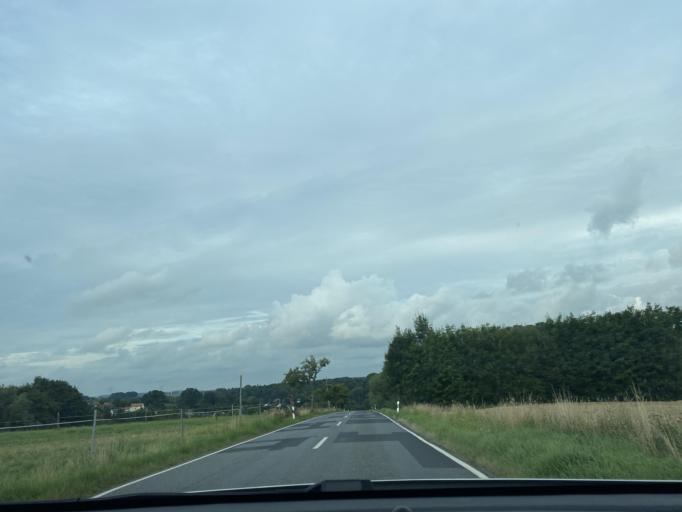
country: DE
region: Saxony
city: Herrnhut
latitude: 51.0194
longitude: 14.7765
